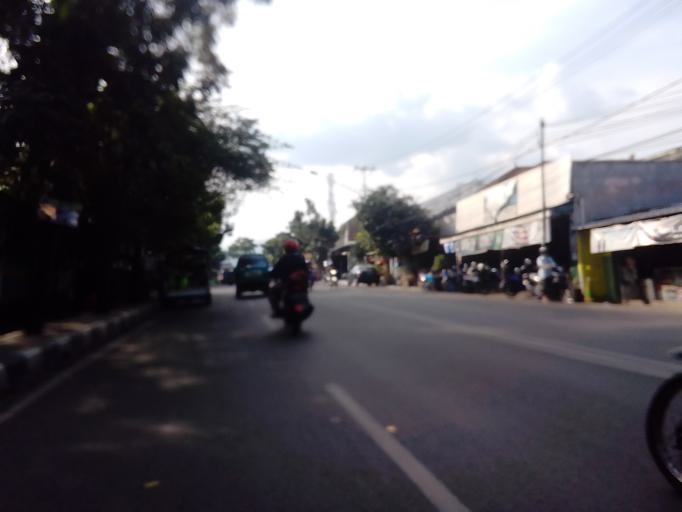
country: ID
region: West Java
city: Cileunyi
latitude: -6.9241
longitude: 107.7103
